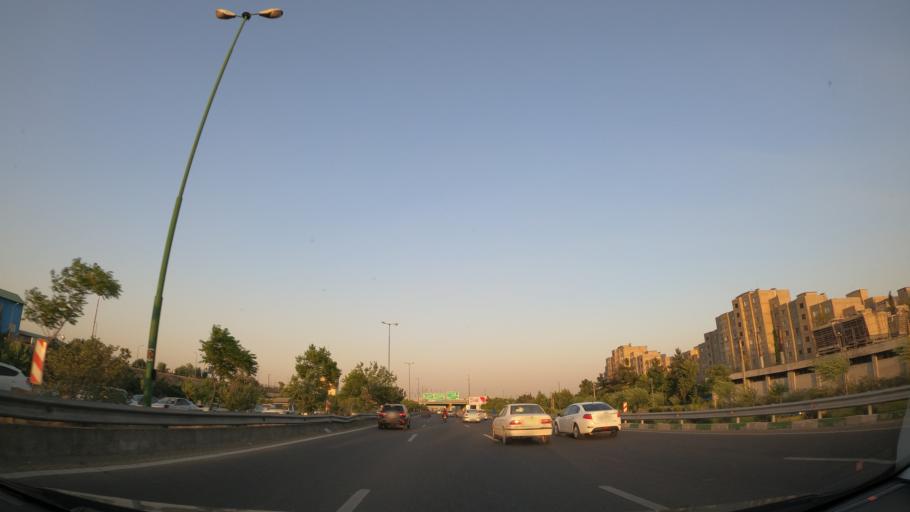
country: IR
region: Tehran
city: Tehran
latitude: 35.7143
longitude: 51.3260
